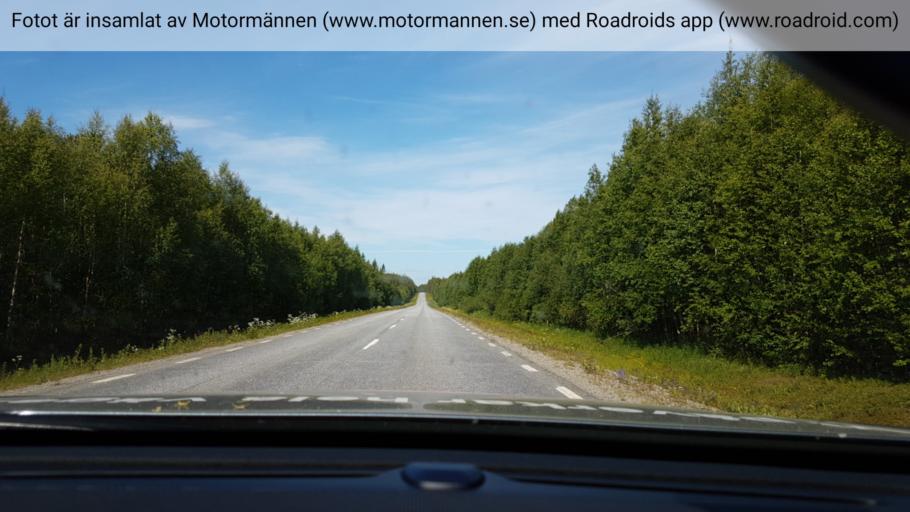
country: SE
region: Vaesterbotten
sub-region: Dorotea Kommun
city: Dorotea
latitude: 64.2509
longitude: 16.5829
